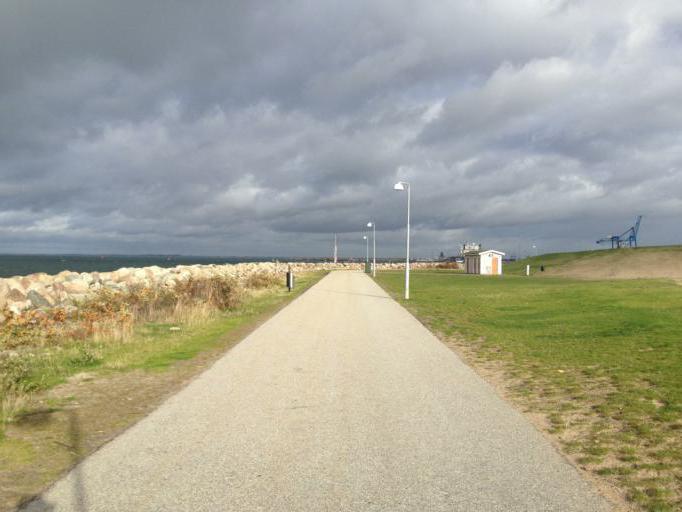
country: SE
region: Skane
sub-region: Malmo
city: Malmoe
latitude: 55.6190
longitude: 12.9767
